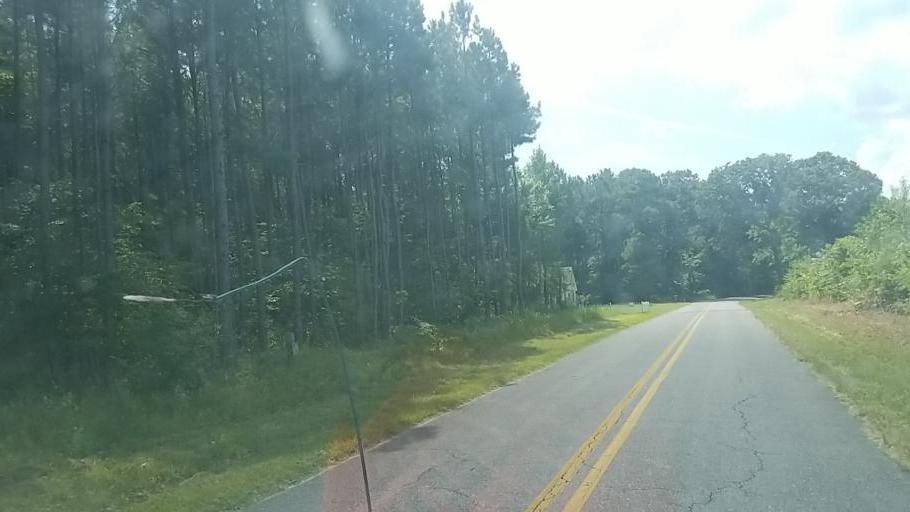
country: US
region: Maryland
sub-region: Worcester County
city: Snow Hill
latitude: 38.2592
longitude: -75.3840
